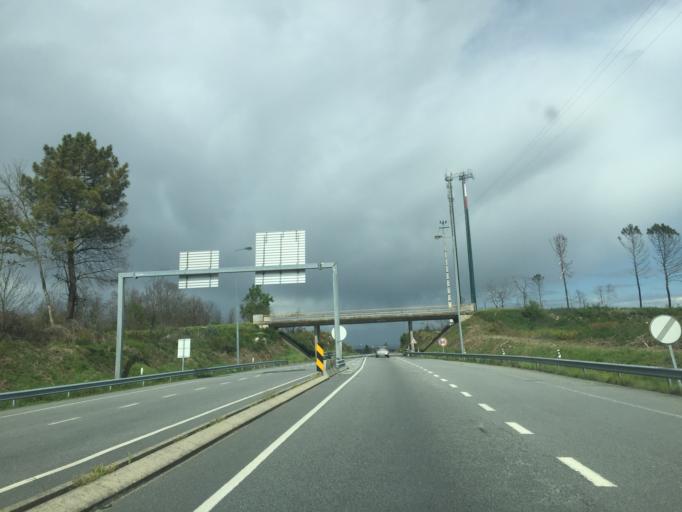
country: PT
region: Viseu
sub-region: Vouzela
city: Vouzela
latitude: 40.6460
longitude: -8.0581
